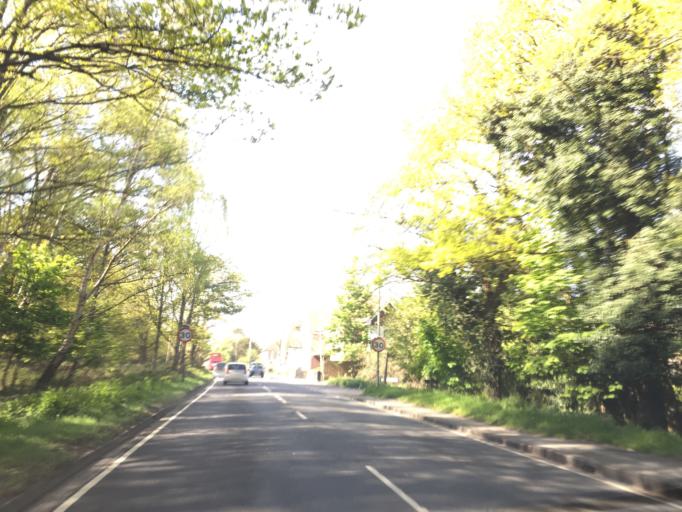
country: GB
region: England
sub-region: Essex
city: Epping
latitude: 51.7076
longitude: 0.1214
